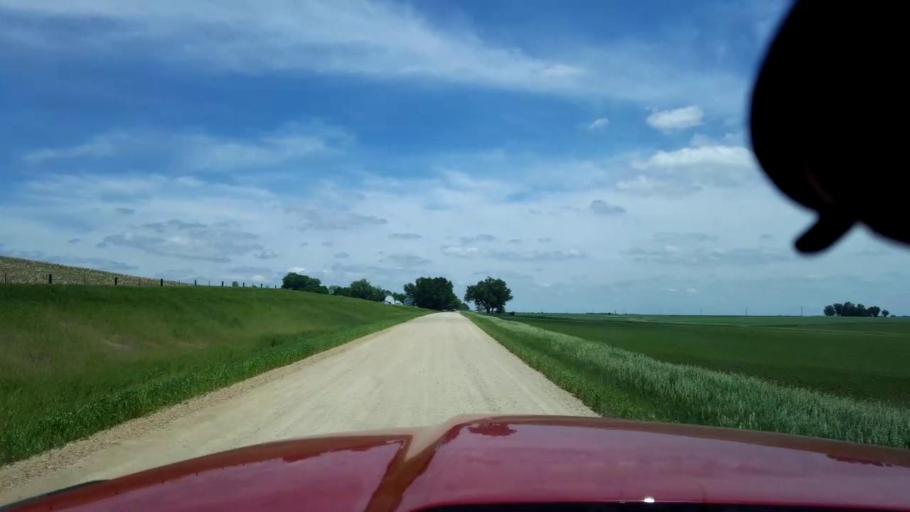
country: US
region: Iowa
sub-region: Linn County
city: Lisbon
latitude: 41.9561
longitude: -91.3650
